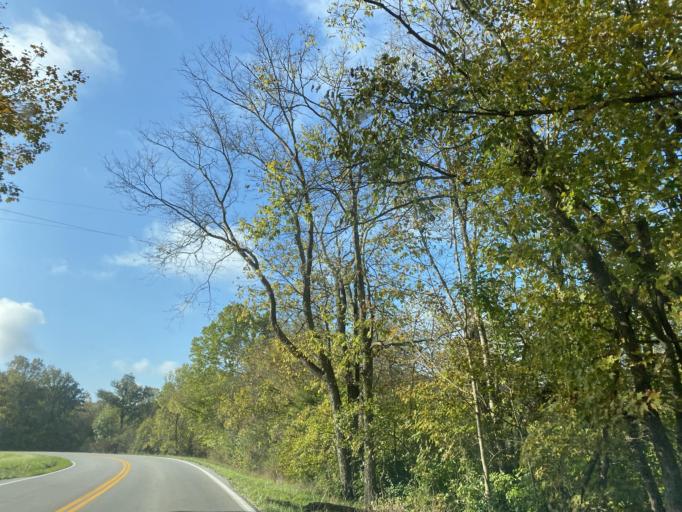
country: US
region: Kentucky
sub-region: Pendleton County
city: Falmouth
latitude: 38.7037
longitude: -84.3043
